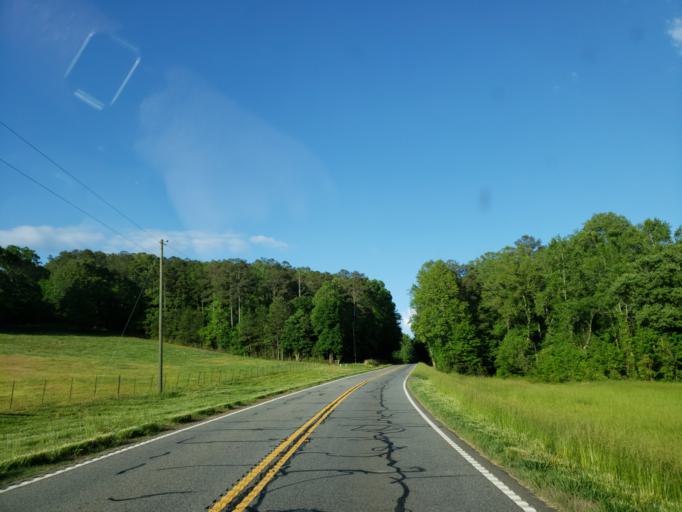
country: US
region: Georgia
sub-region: Bartow County
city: Rydal
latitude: 34.3469
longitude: -84.6058
